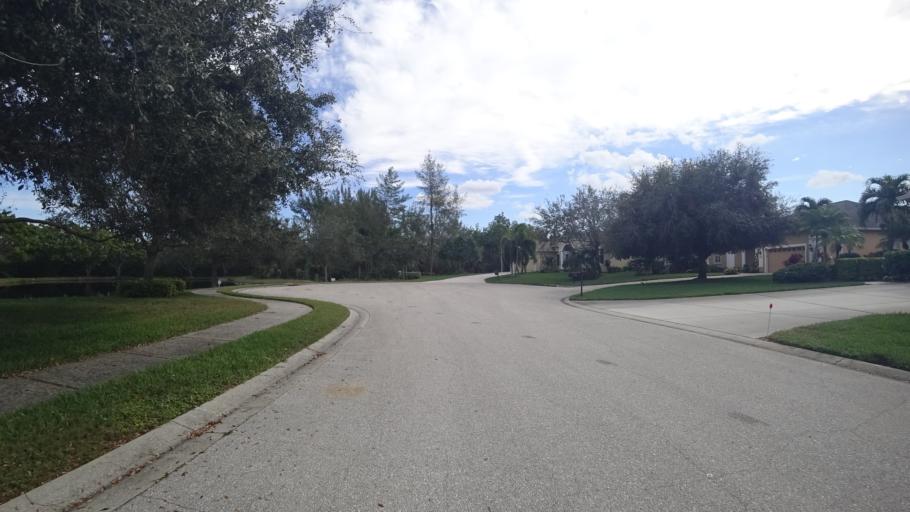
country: US
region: Florida
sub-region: Manatee County
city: West Bradenton
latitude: 27.5056
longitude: -82.6428
